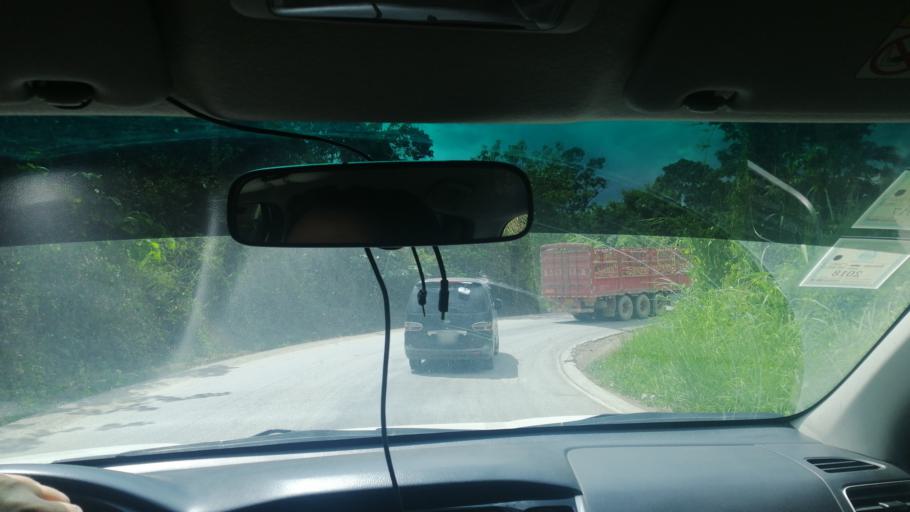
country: LA
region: Loungnamtha
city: Louang Namtha
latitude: 21.0419
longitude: 101.6500
